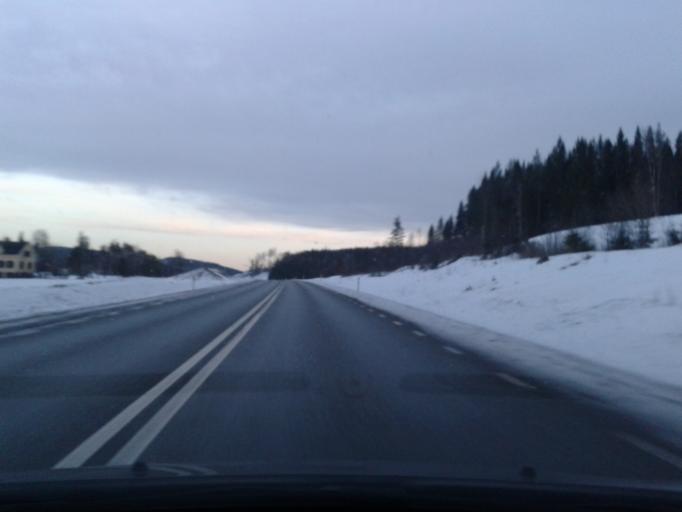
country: SE
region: Vaesternorrland
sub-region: Kramfors Kommun
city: Bollstabruk
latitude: 63.0382
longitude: 17.6517
